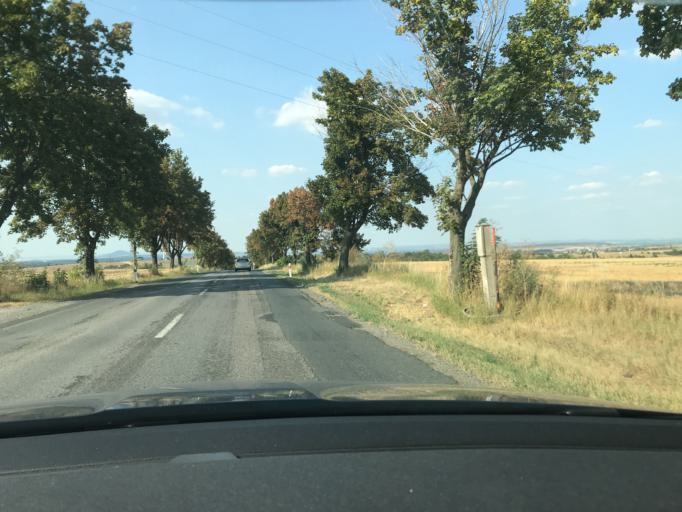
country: CZ
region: Central Bohemia
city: Kralupy nad Vltavou
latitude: 50.2120
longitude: 14.3163
